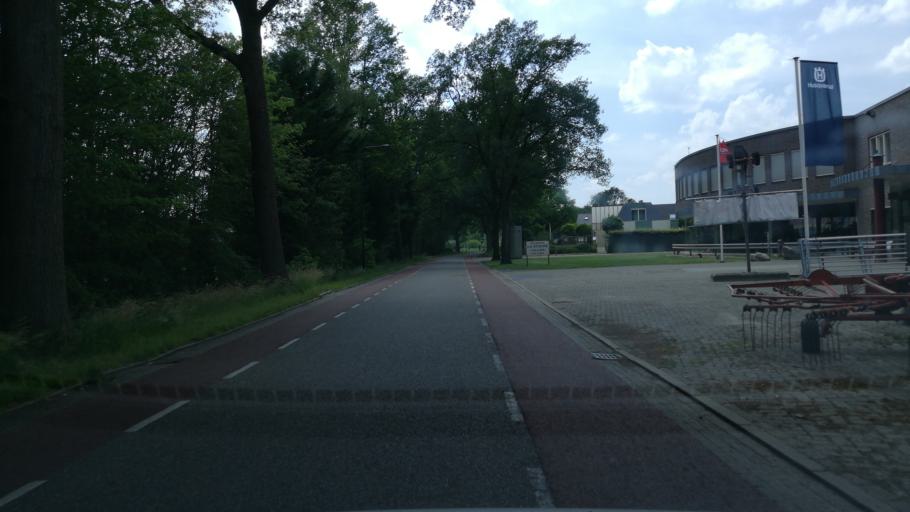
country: NL
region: Overijssel
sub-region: Gemeente Dalfsen
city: Dalfsen
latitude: 52.5083
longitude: 6.2696
